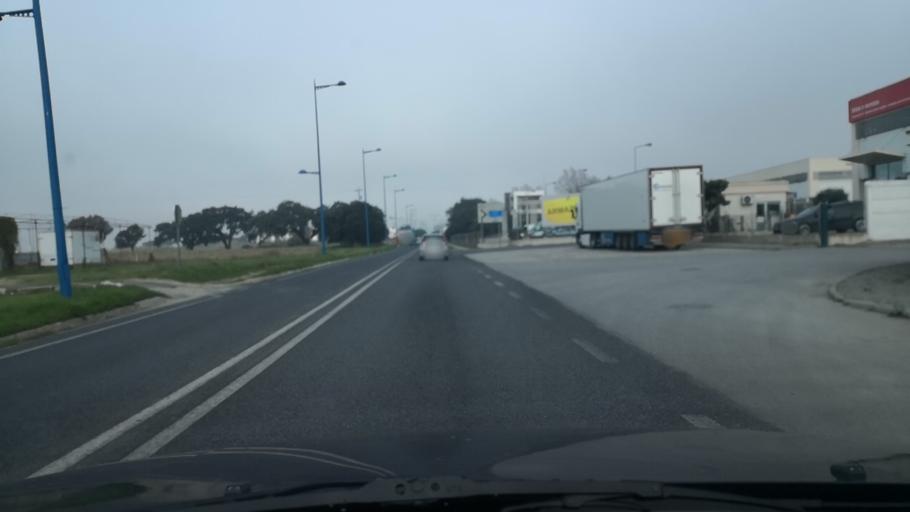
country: PT
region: Setubal
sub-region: Montijo
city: Montijo
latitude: 38.6905
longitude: -8.9479
